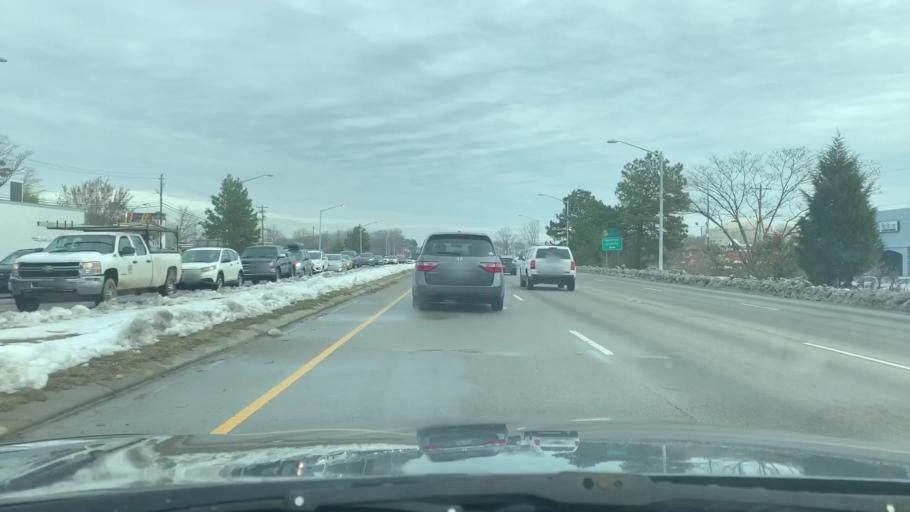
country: US
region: North Carolina
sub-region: Orange County
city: Chapel Hill
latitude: 35.9515
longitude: -78.9975
